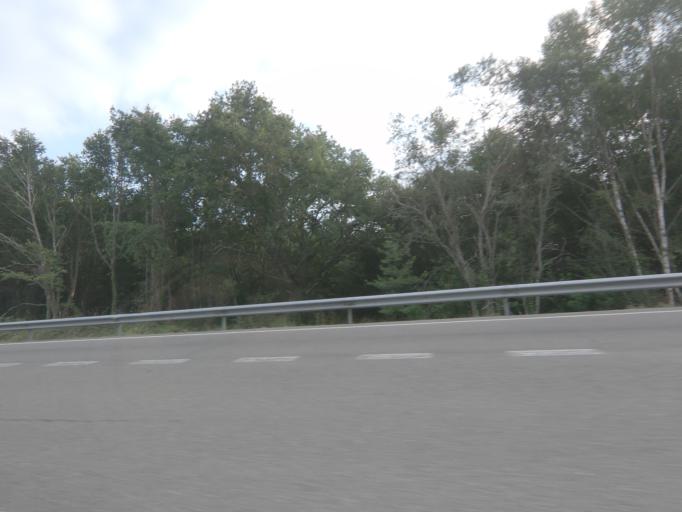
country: ES
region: Galicia
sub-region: Provincia de Ourense
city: Taboadela
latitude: 42.2208
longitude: -7.8419
